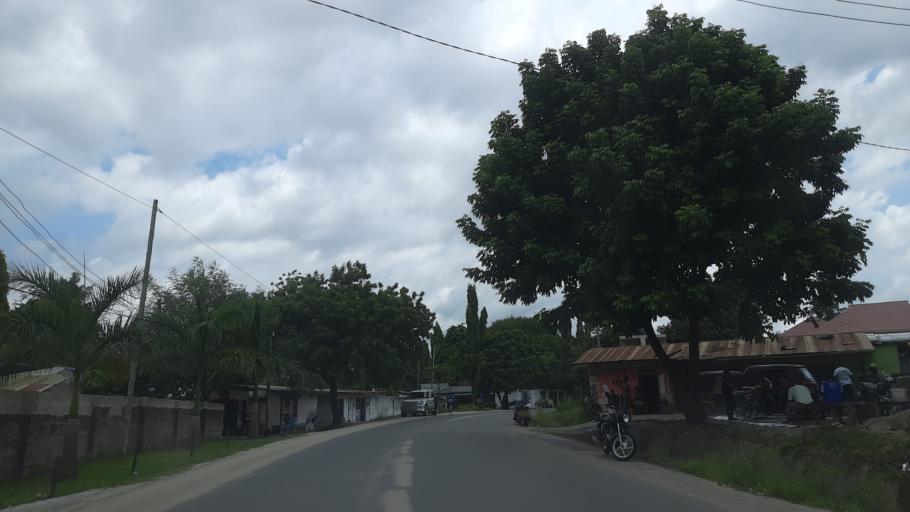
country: TZ
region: Dar es Salaam
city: Magomeni
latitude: -6.7812
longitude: 39.2399
